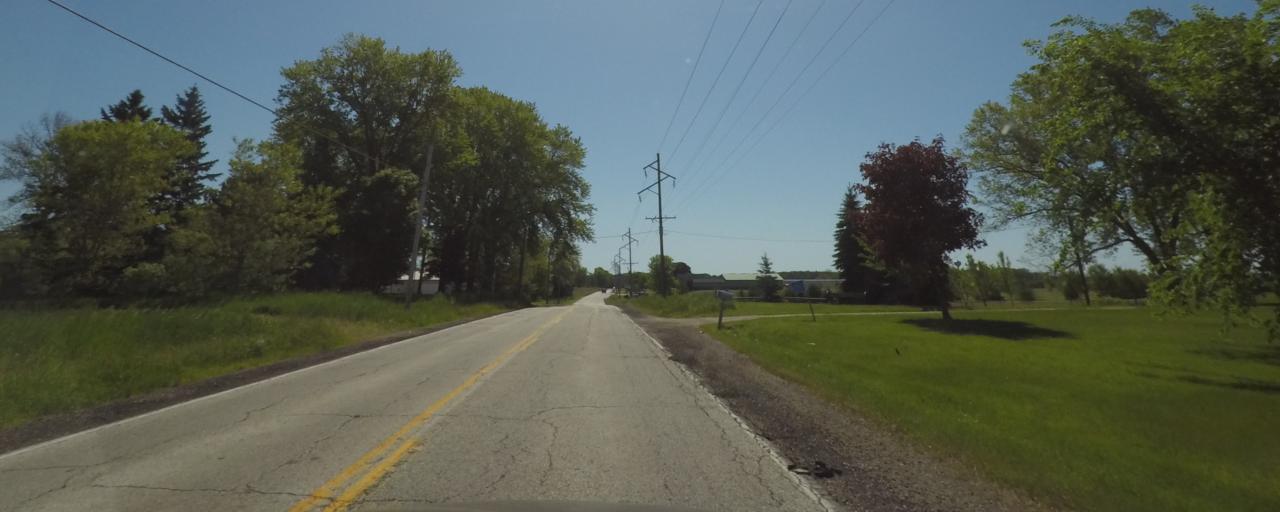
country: US
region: Wisconsin
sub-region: Sheboygan County
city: Sheboygan Falls
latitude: 43.7410
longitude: -87.8573
